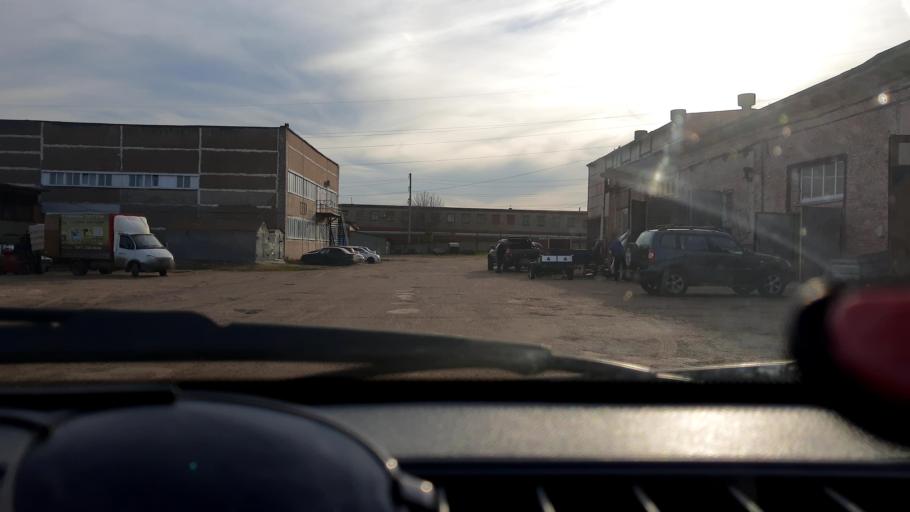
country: RU
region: Bashkortostan
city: Ufa
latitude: 54.8289
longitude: 56.1130
